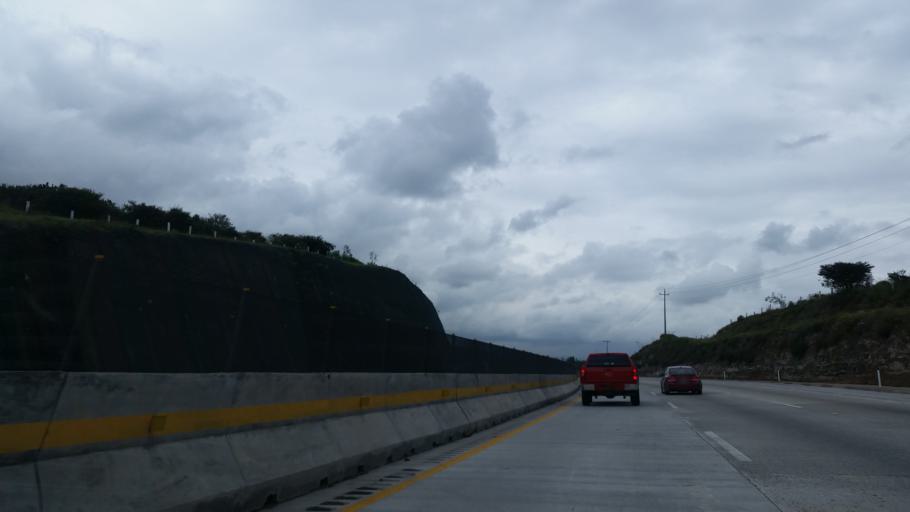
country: MX
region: Hidalgo
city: Tepeji de Ocampo
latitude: 19.9097
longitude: -99.3540
